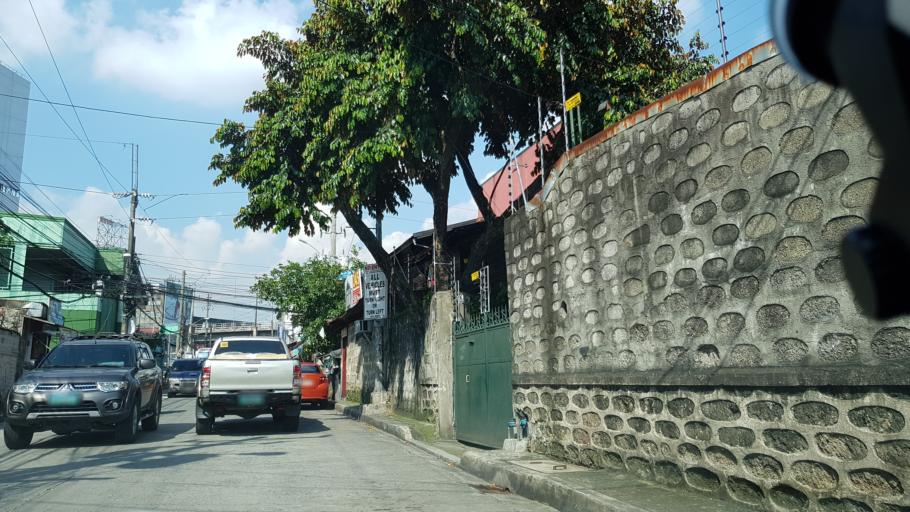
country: PH
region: Metro Manila
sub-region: Quezon City
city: Quezon City
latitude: 14.6226
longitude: 121.0483
